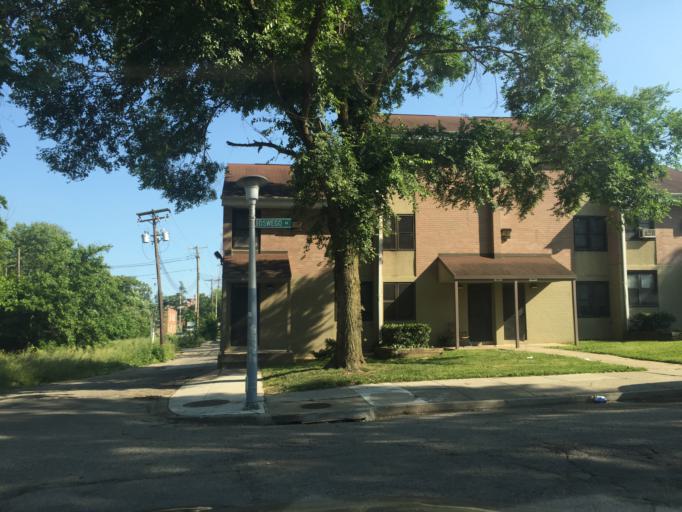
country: US
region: Maryland
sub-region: Baltimore County
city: Lochearn
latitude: 39.3368
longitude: -76.6604
